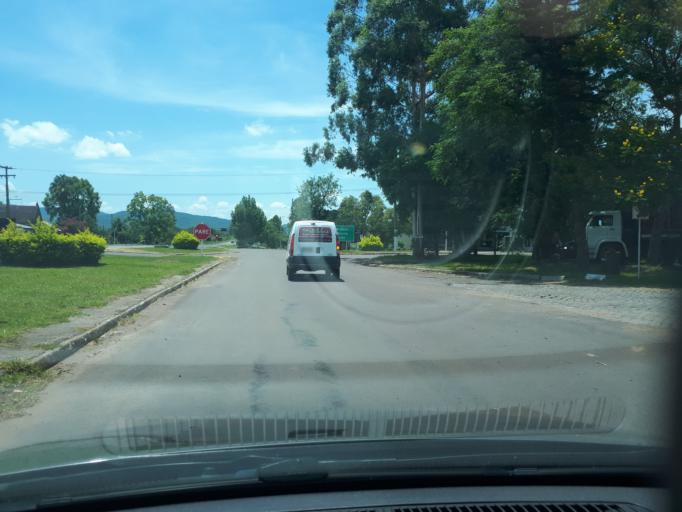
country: BR
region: Rio Grande do Sul
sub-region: Candelaria
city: Candelaria
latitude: -29.7323
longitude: -52.9465
